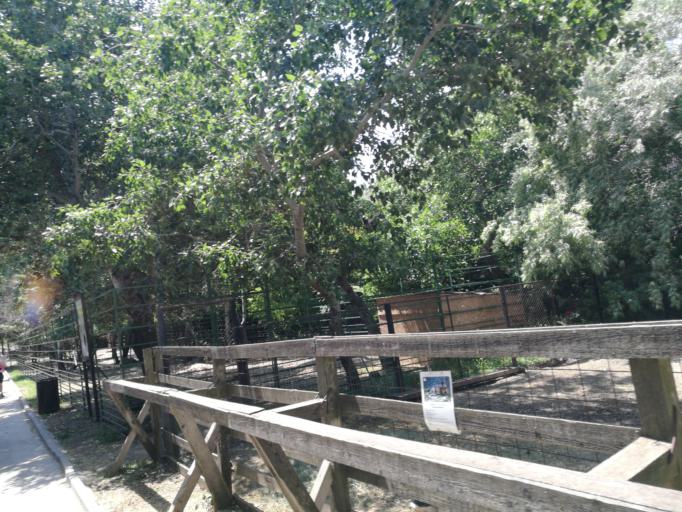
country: RO
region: Constanta
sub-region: Municipiul Constanta
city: Constanta
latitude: 44.2044
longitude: 28.6393
